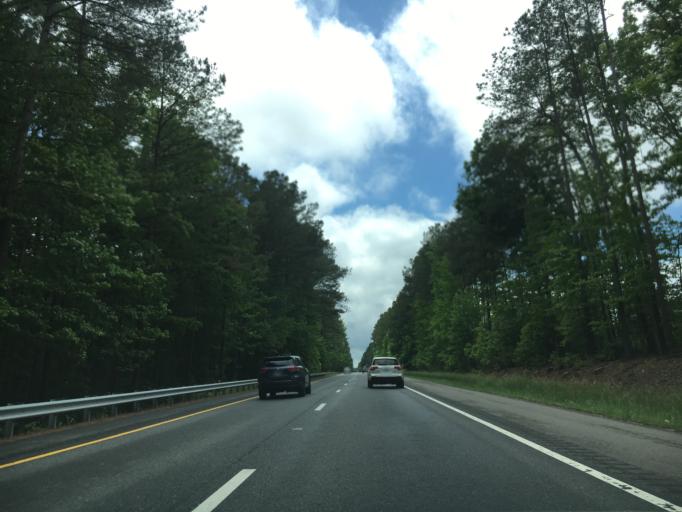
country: US
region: Virginia
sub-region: Brunswick County
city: Lawrenceville
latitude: 36.8284
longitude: -77.9477
